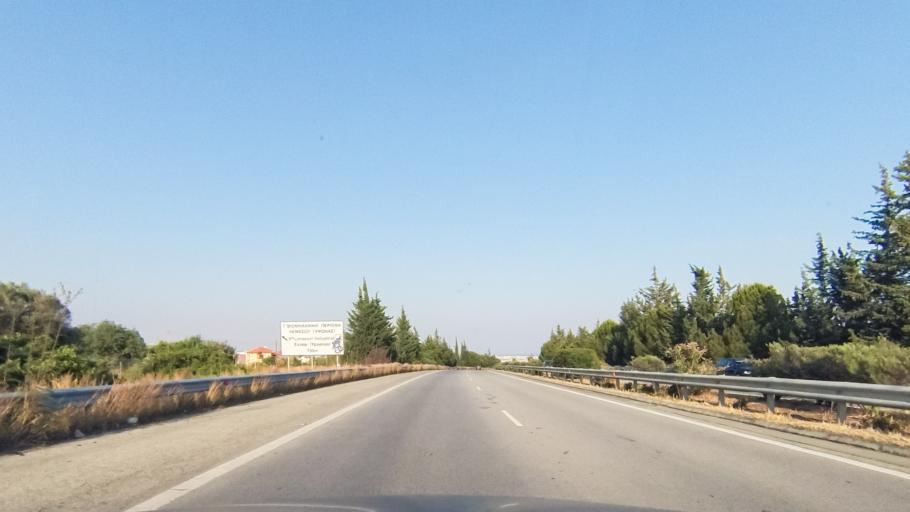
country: CY
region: Limassol
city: Ypsonas
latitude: 34.6970
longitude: 32.9601
